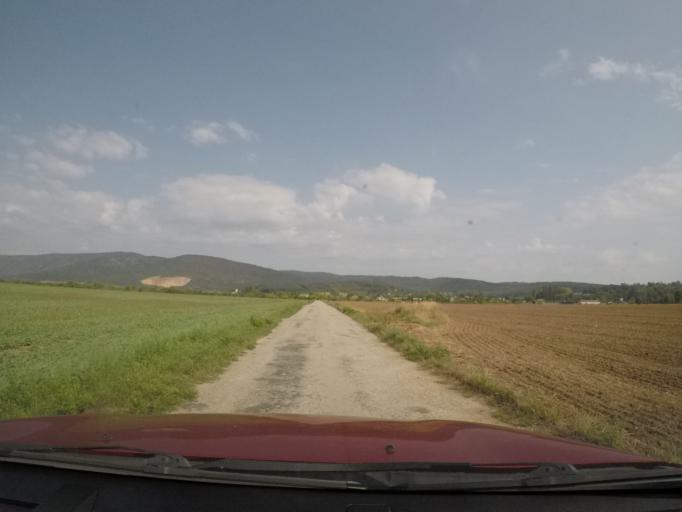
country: SK
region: Kosicky
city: Moldava nad Bodvou
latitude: 48.6011
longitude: 20.9536
